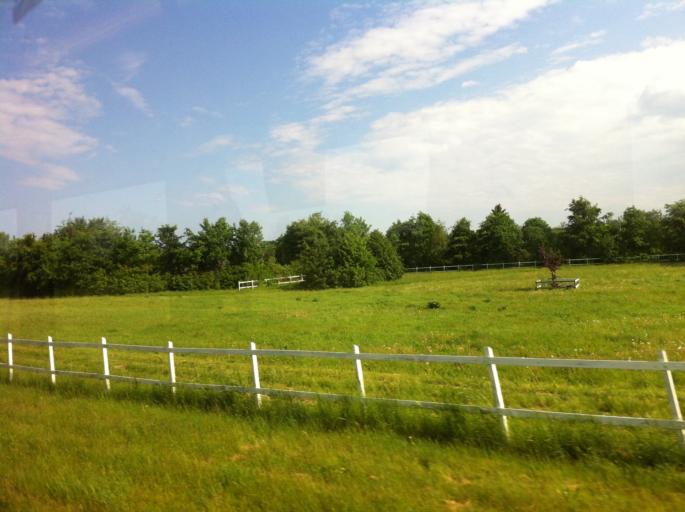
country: DK
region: Capital Region
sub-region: Helsingor Kommune
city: Hornbaek
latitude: 56.0811
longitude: 12.4727
